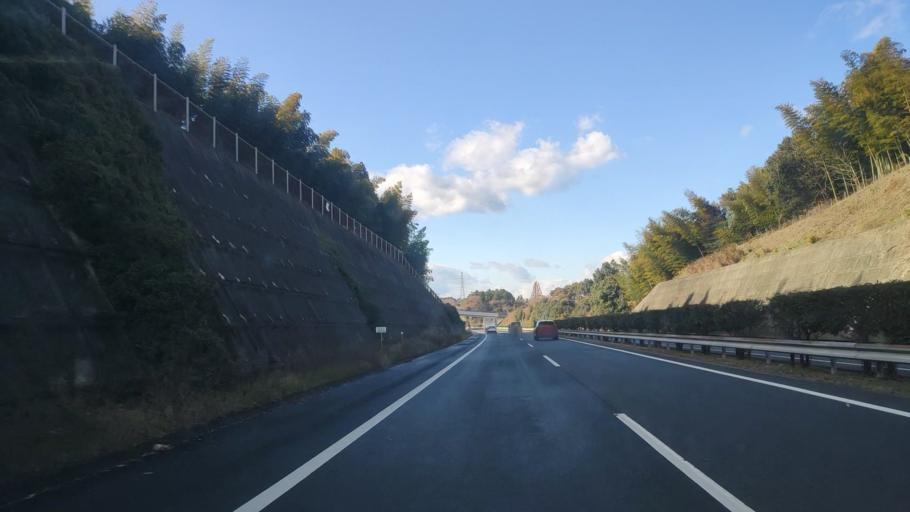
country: JP
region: Ehime
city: Saijo
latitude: 33.9100
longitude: 133.2486
